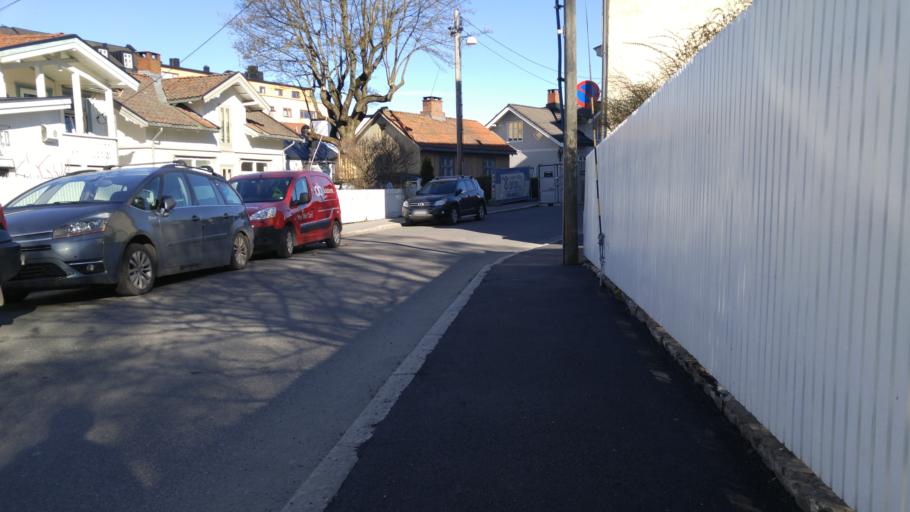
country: NO
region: Oslo
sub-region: Oslo
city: Oslo
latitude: 59.9071
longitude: 10.7930
